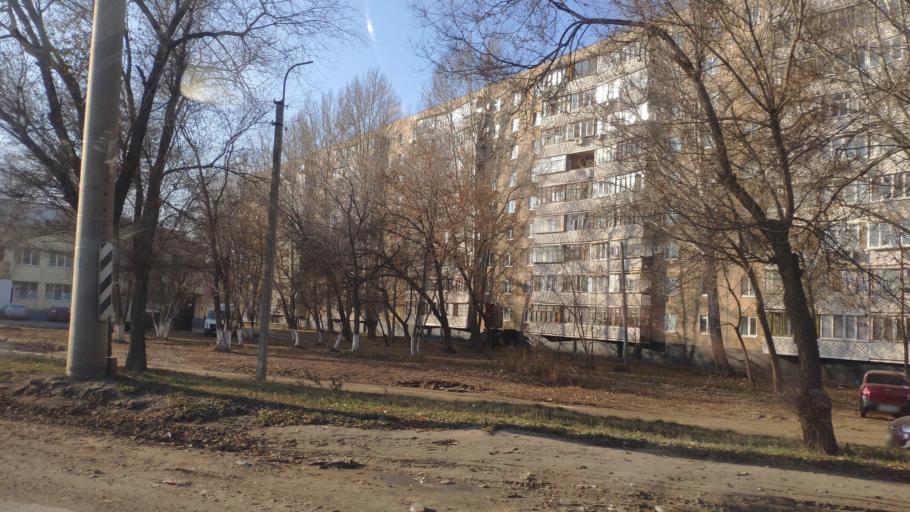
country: RU
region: Orenburg
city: Prigorodnyy
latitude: 51.7779
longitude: 55.1907
